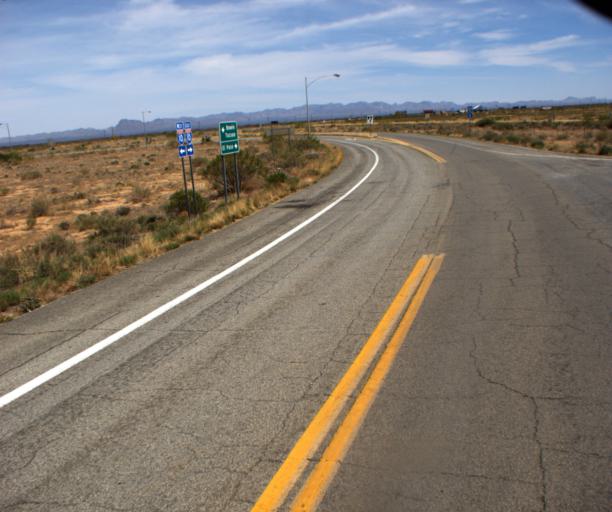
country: US
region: Arizona
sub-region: Cochise County
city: Willcox
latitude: 32.3160
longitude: -109.4478
